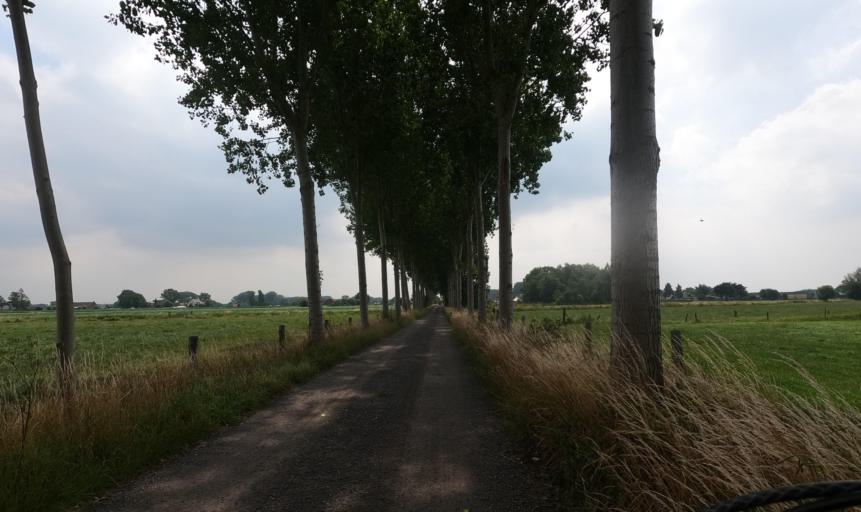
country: BE
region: Flanders
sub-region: Provincie Vlaams-Brabant
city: Kapelle-op-den-Bos
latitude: 51.0016
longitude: 4.3387
